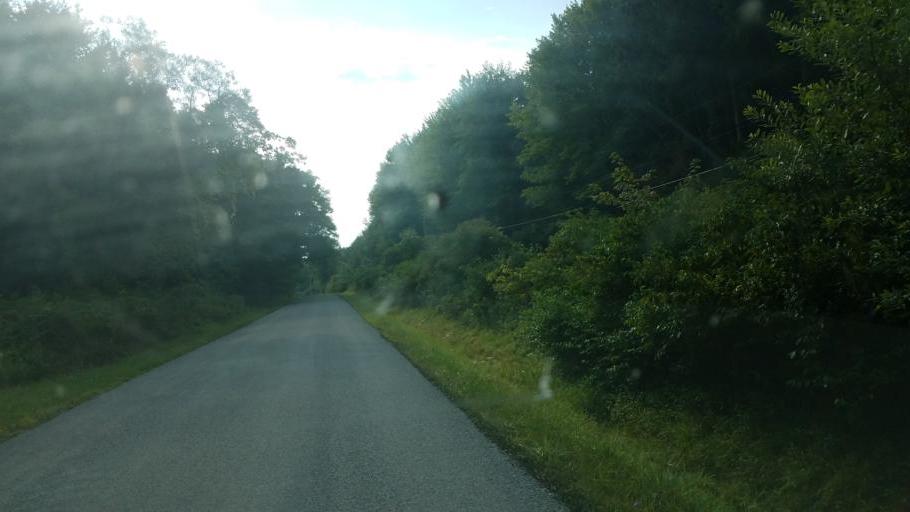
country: US
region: Pennsylvania
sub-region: Crawford County
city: Pymatuning Central
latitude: 41.6203
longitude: -80.4574
